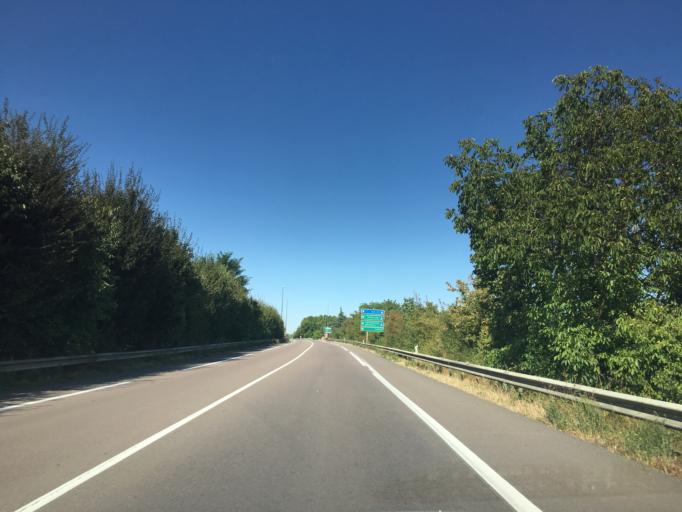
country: FR
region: Bourgogne
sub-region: Departement de l'Yonne
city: Maillot
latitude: 48.1874
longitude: 3.3092
